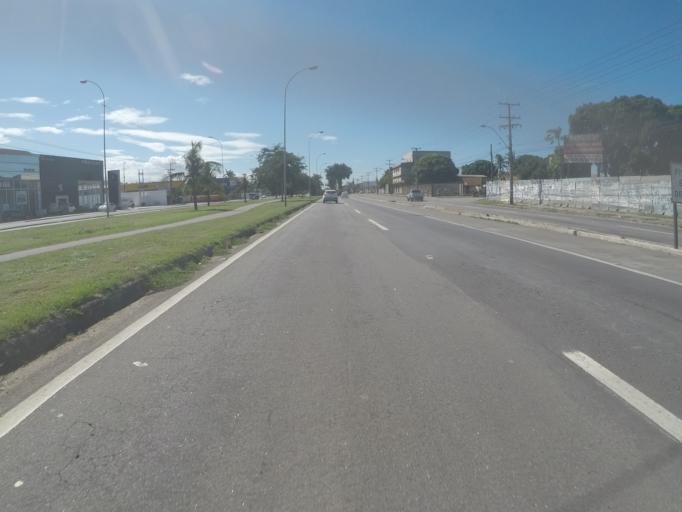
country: BR
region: Espirito Santo
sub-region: Serra
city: Serra
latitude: -20.2106
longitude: -40.2695
